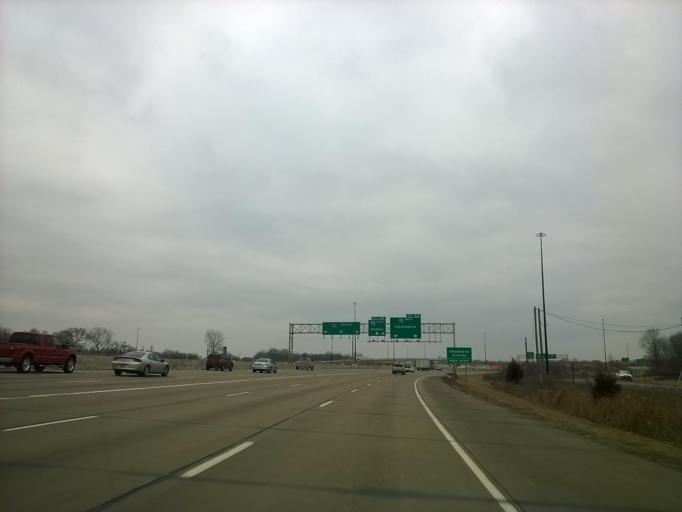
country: US
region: Indiana
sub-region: Marion County
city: Warren Park
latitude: 39.8042
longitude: -86.0319
